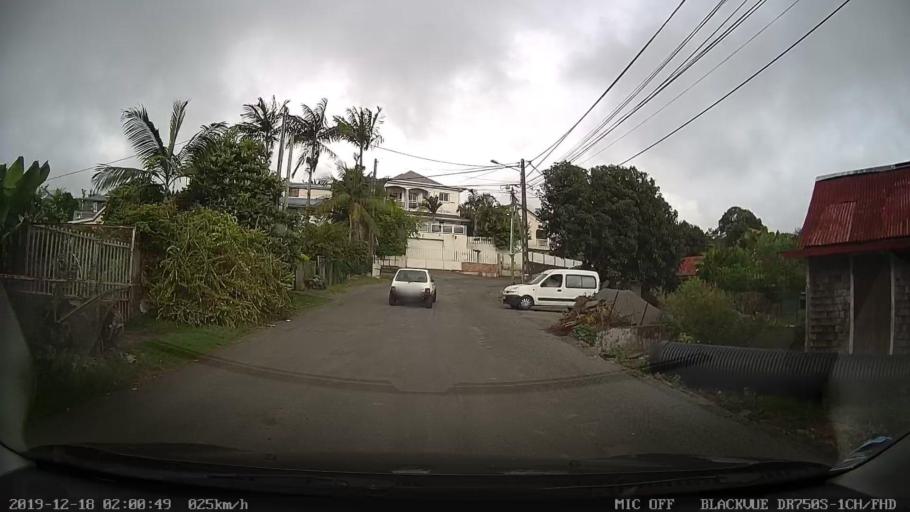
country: RE
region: Reunion
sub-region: Reunion
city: Le Tampon
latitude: -21.2525
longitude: 55.5190
